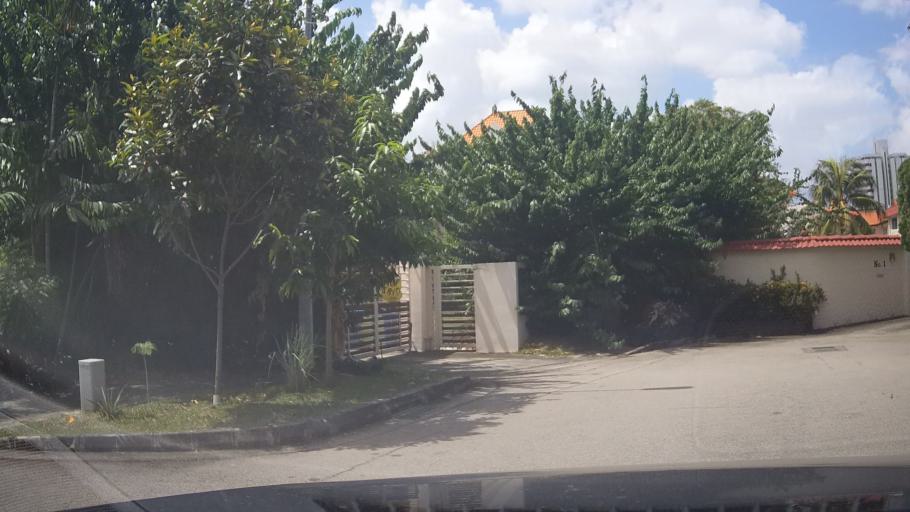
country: SG
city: Singapore
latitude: 1.3104
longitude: 103.9215
